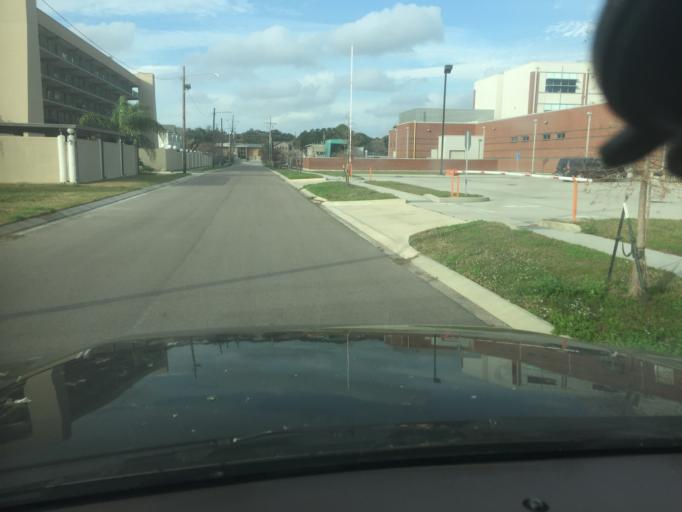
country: US
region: Louisiana
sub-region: Orleans Parish
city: New Orleans
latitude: 29.9971
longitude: -90.0842
